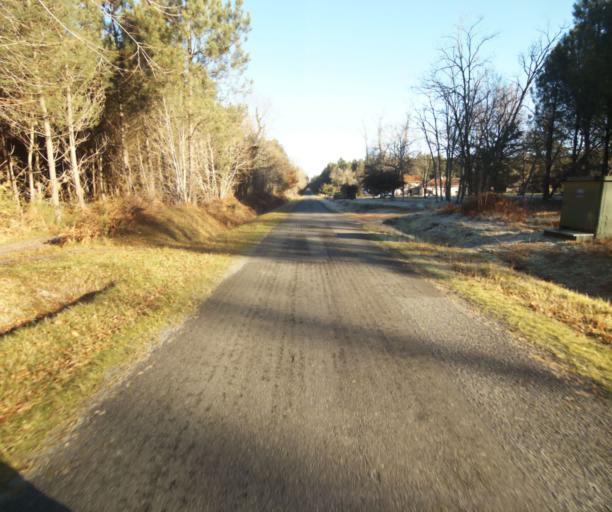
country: FR
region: Aquitaine
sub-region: Departement des Landes
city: Gabarret
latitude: 44.1153
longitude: 0.0818
